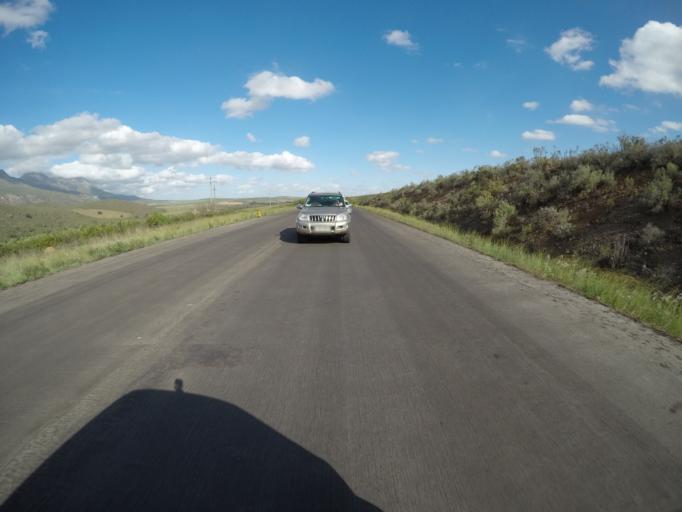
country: ZA
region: Western Cape
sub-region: Cape Winelands District Municipality
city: Ashton
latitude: -33.9301
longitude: 20.2082
